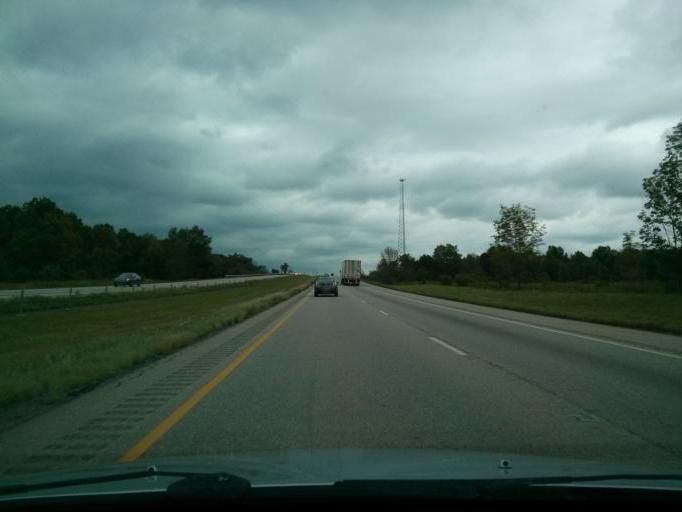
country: US
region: Ohio
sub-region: Mahoning County
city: Craig Beach
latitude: 41.1030
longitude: -81.0287
